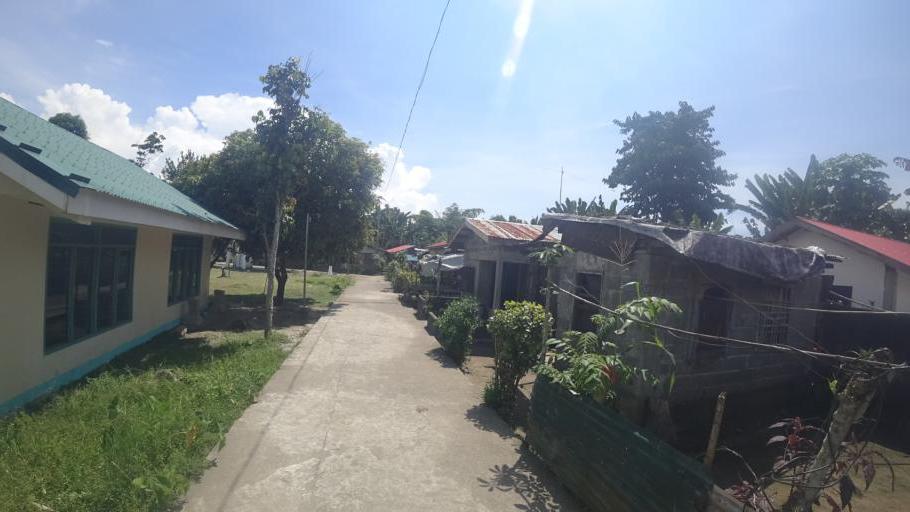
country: PH
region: Eastern Visayas
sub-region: Province of Leyte
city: Jaro
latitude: 11.1978
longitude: 124.8106
